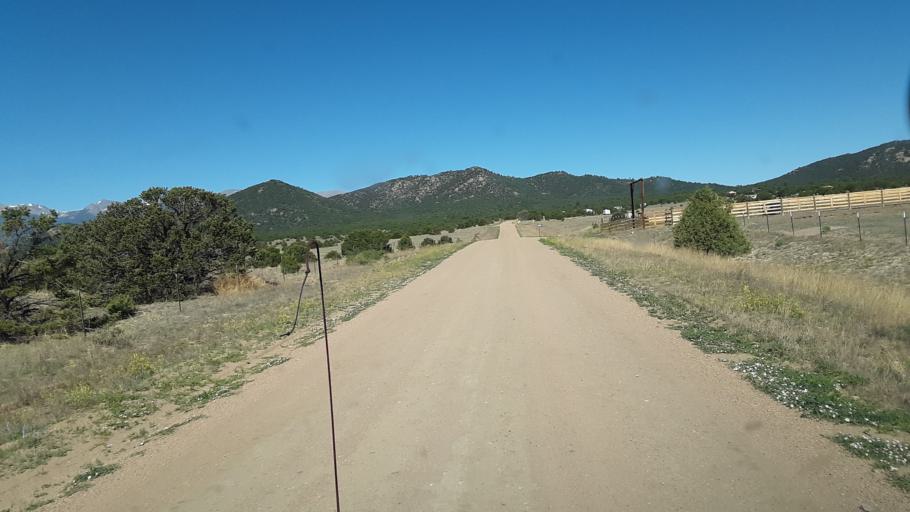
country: US
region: Colorado
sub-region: Custer County
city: Westcliffe
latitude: 38.2851
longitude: -105.5175
